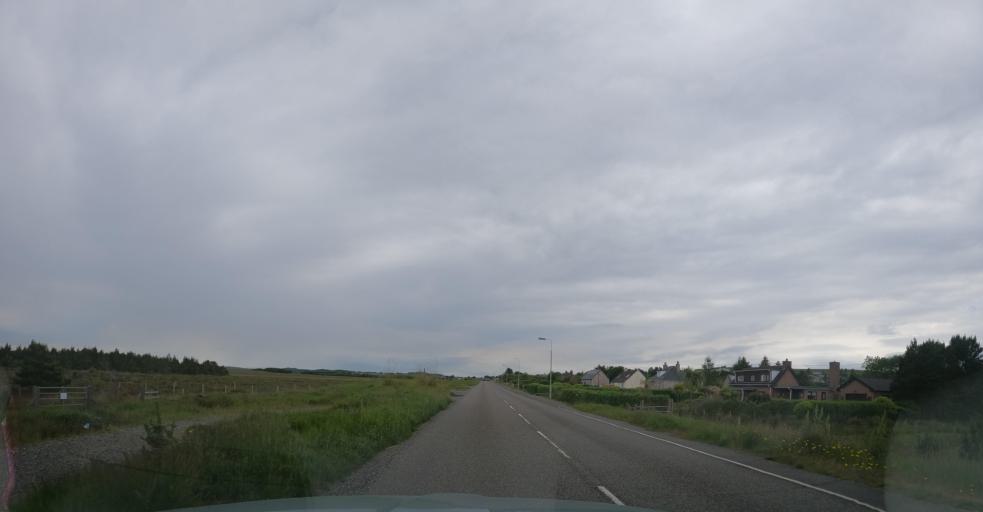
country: GB
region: Scotland
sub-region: Eilean Siar
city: Isle of Lewis
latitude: 58.2403
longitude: -6.3760
